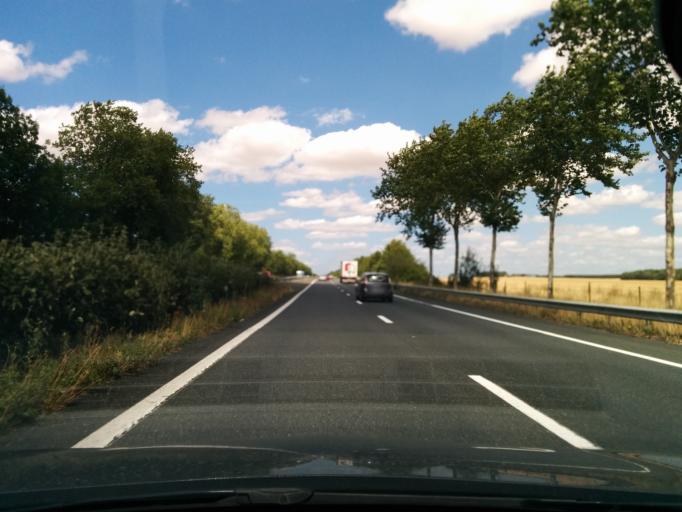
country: FR
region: Centre
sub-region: Departement de l'Indre
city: Montierchaume
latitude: 46.9238
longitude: 1.7435
